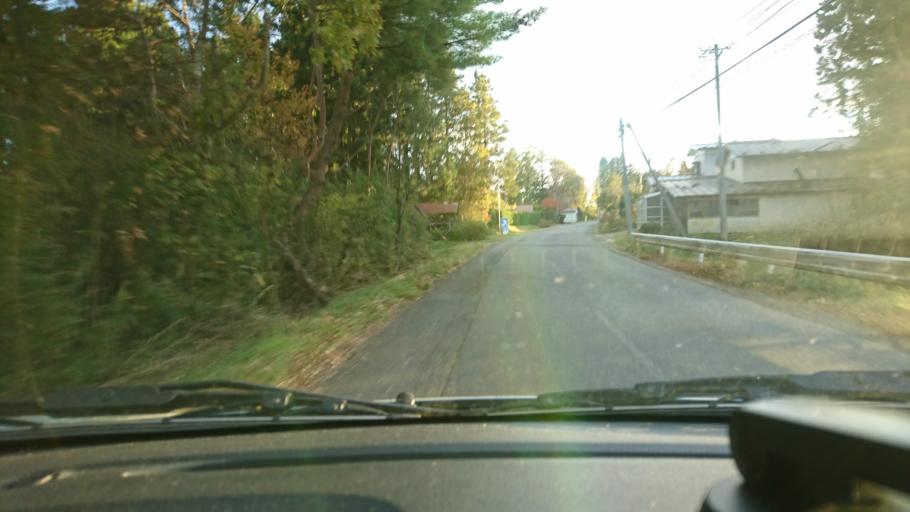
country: JP
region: Iwate
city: Ichinoseki
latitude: 38.7951
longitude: 141.1925
